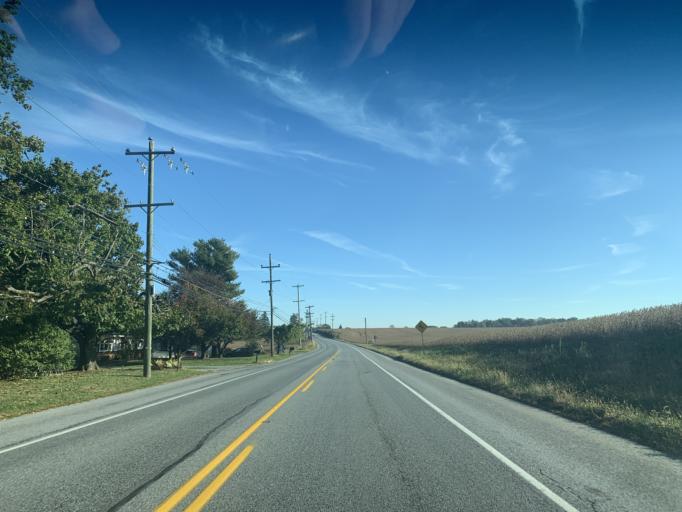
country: US
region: Pennsylvania
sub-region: Chester County
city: Oxford
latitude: 39.8244
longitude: -75.9603
